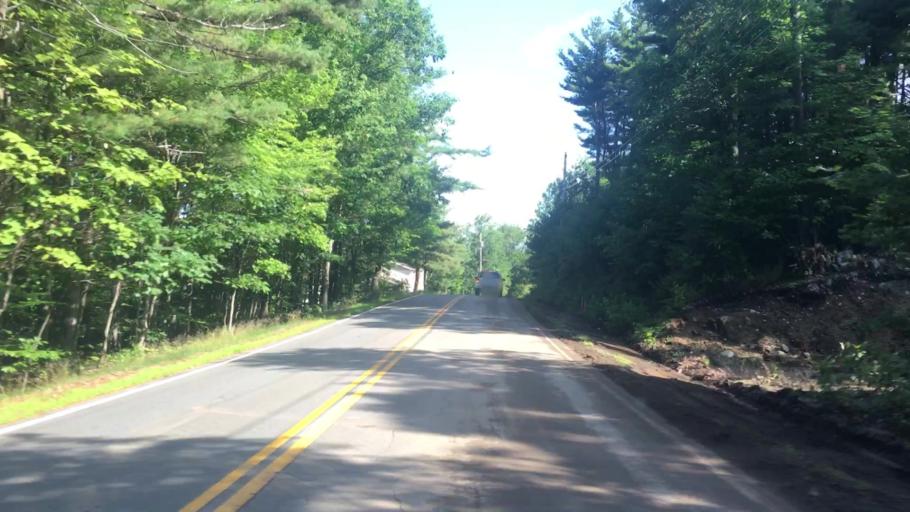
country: US
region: New Hampshire
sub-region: Belknap County
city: Gilford
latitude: 43.5342
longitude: -71.3468
